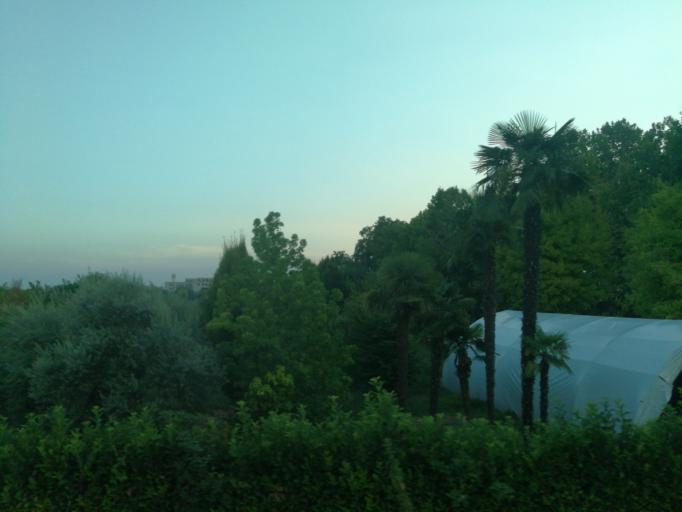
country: IT
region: Lombardy
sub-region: Provincia di Bergamo
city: Orio al Serio
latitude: 45.6679
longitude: 9.6867
